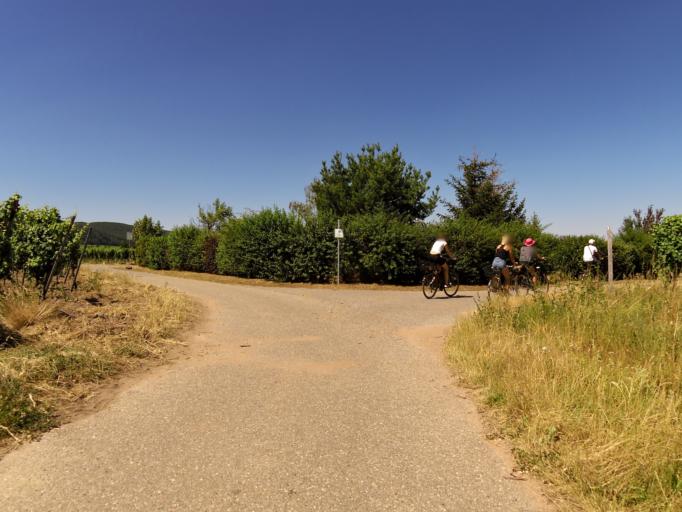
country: DE
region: Rheinland-Pfalz
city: Ruppertsberg
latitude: 49.3915
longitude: 8.1842
